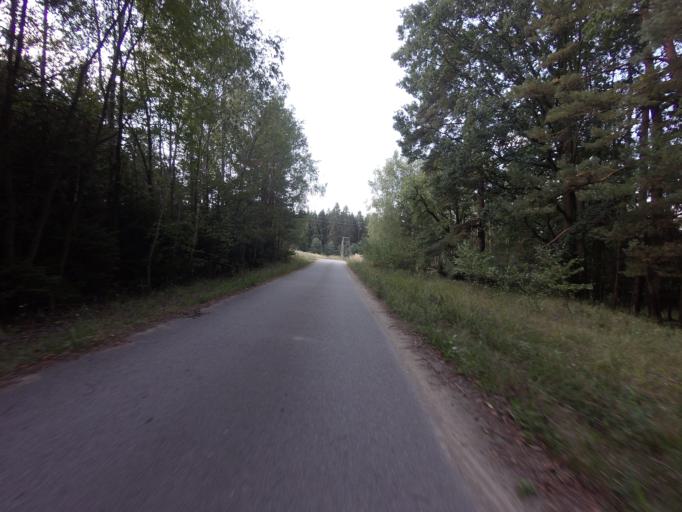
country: CZ
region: Jihocesky
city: Tyn nad Vltavou
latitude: 49.1761
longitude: 14.4398
